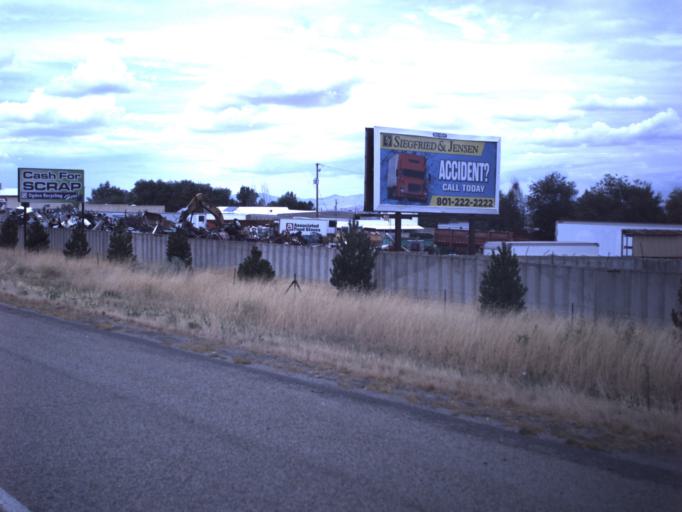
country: US
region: Utah
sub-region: Weber County
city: Riverdale
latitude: 41.2041
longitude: -112.0093
